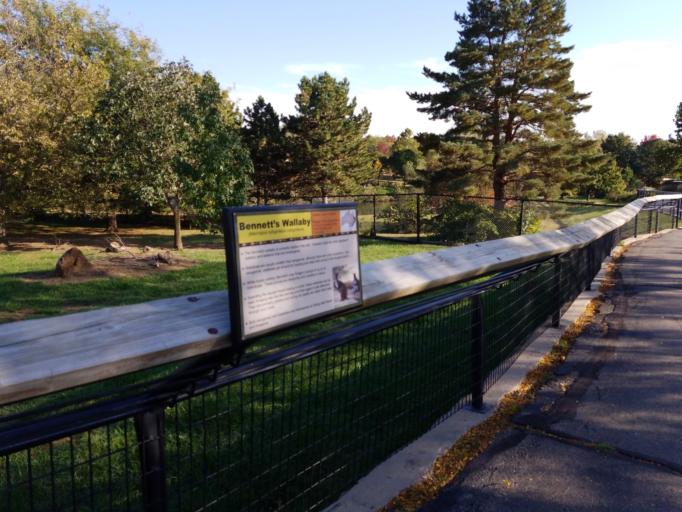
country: US
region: Kansas
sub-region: Saline County
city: Salina
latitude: 38.8544
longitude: -97.7659
